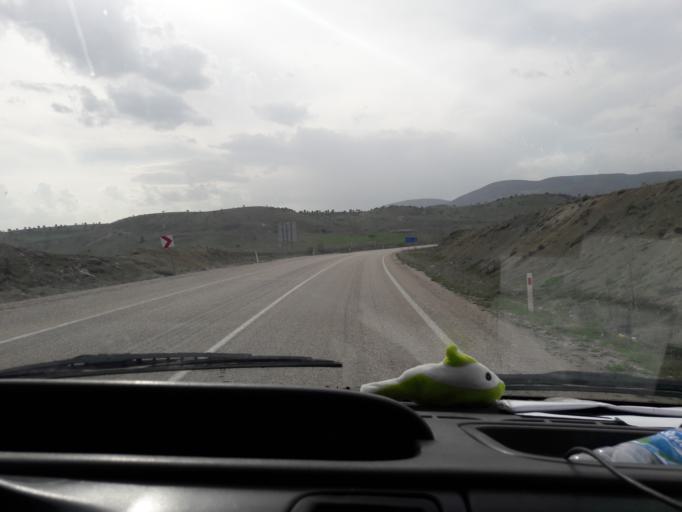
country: TR
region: Gumushane
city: Siran
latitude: 40.1604
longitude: 39.0144
